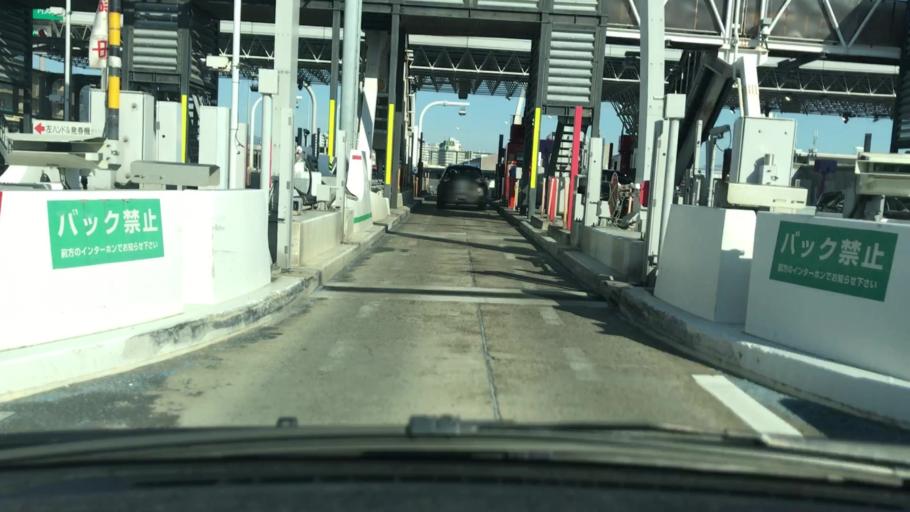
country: JP
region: Hyogo
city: Nishinomiya-hama
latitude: 34.7325
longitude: 135.3589
